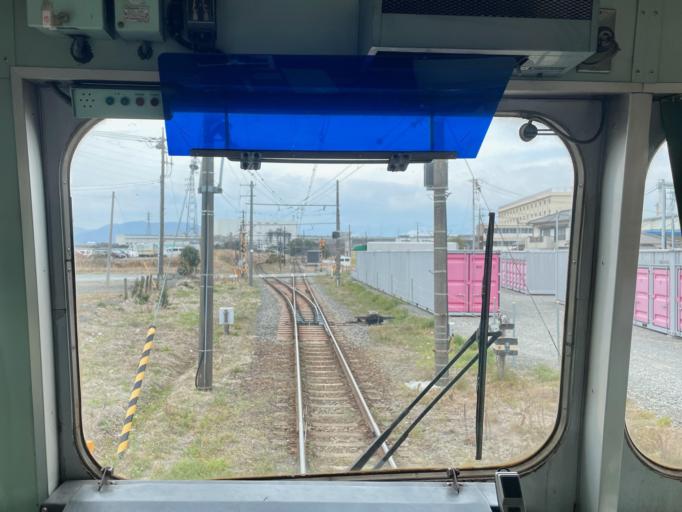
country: JP
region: Shizuoka
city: Fuji
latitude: 35.1616
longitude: 138.7147
